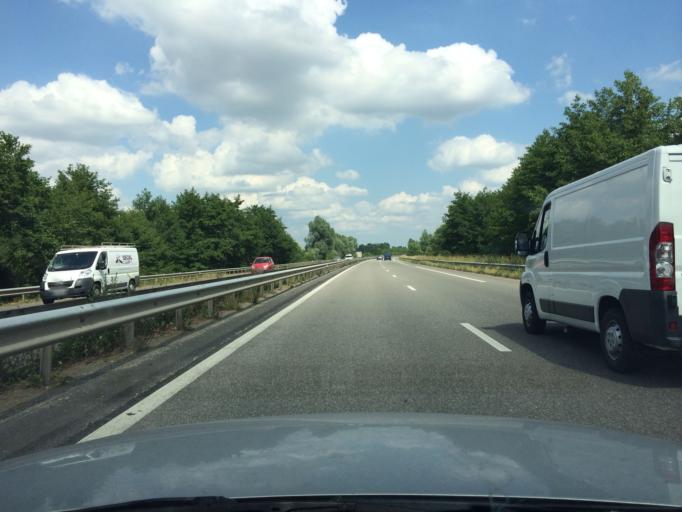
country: FR
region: Lorraine
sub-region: Departement de la Moselle
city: Reding
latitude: 48.7373
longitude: 7.0918
